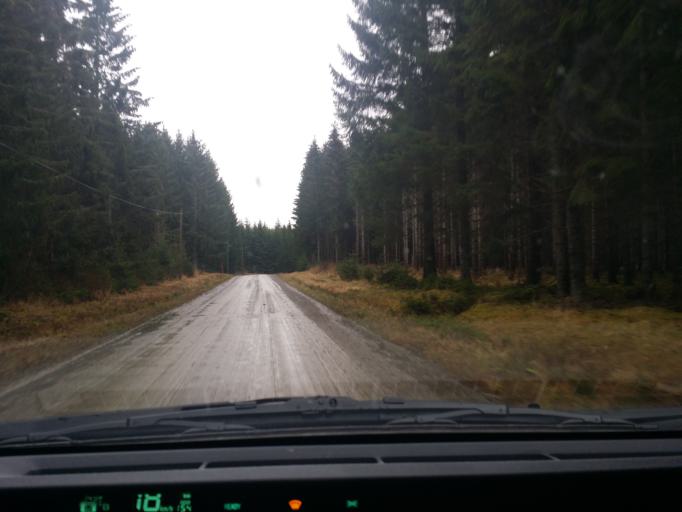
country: SE
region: Vaestmanland
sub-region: Vasteras
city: Skultuna
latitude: 59.7736
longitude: 16.3263
